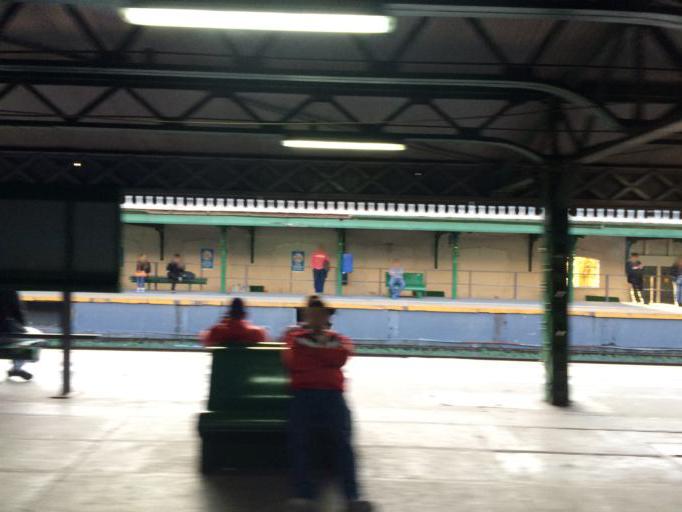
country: AR
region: Buenos Aires
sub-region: Partido de Lanus
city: Lanus
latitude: -34.7071
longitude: -58.3905
